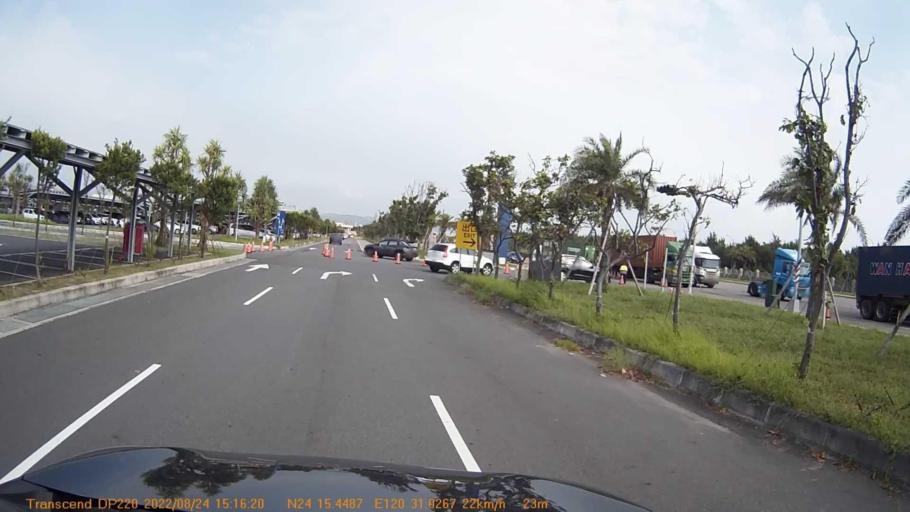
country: TW
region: Taiwan
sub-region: Changhua
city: Chang-hua
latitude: 24.2574
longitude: 120.5172
